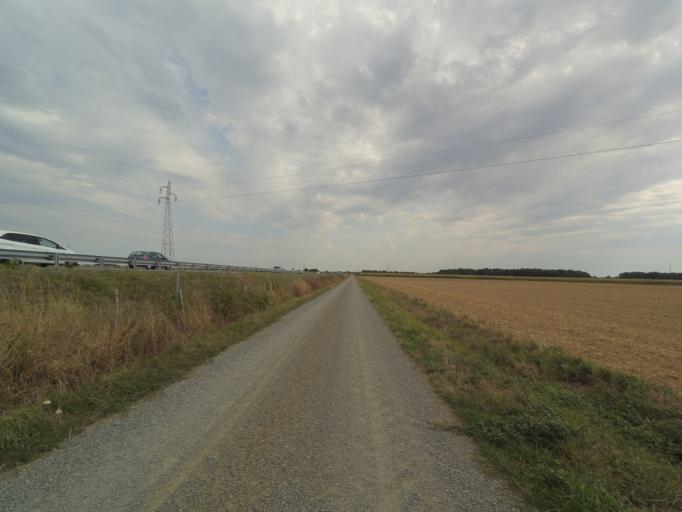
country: FR
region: Pays de la Loire
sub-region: Departement de la Vendee
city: Bouffere
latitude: 46.9795
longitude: -1.3746
